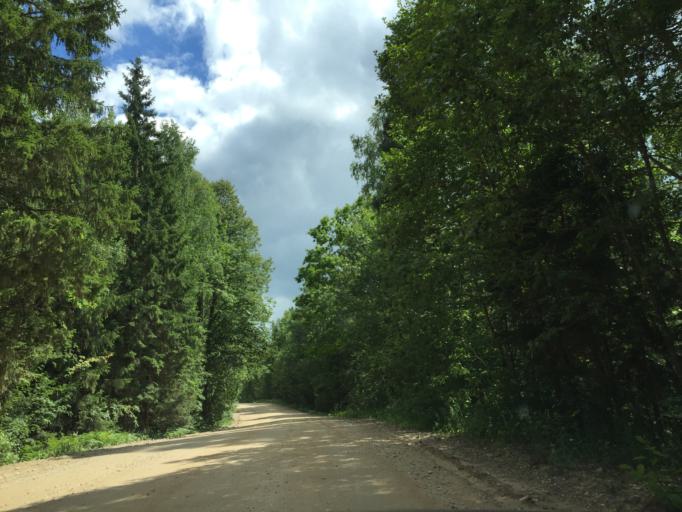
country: LV
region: Ropazu
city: Ropazi
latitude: 56.9140
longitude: 24.7520
